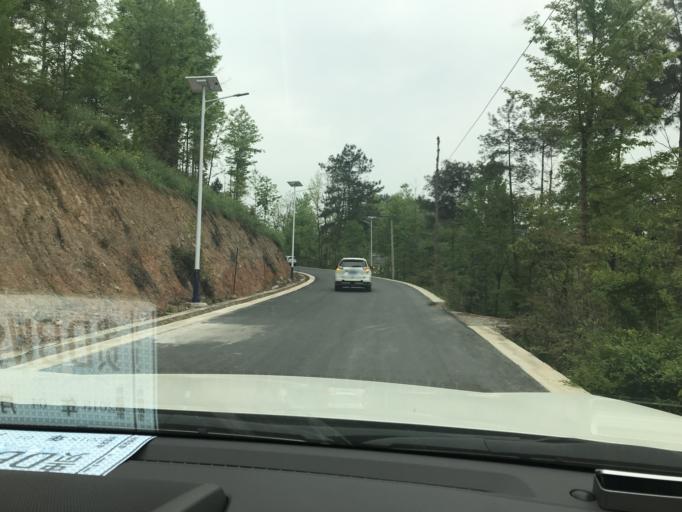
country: CN
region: Guizhou Sheng
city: Tongjing
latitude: 28.3061
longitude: 108.2725
